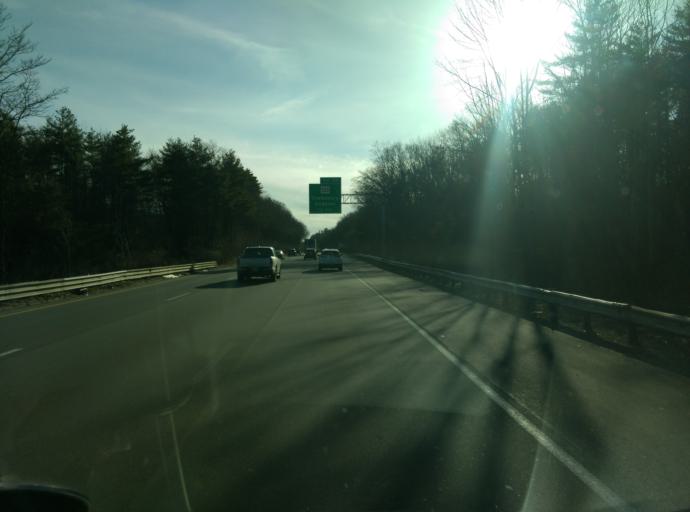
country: US
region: Massachusetts
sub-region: Middlesex County
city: Tewksbury
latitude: 42.6493
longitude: -71.2177
